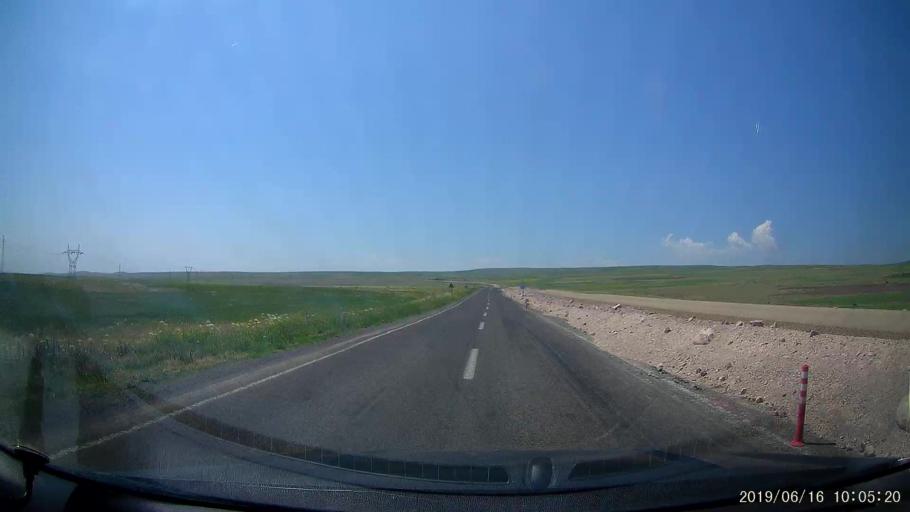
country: TR
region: Kars
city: Digor
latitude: 40.2717
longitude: 43.5381
